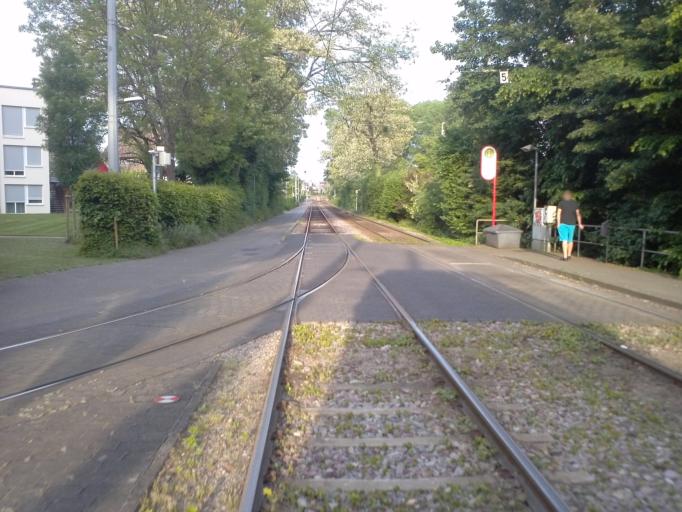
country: DE
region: Baden-Wuerttemberg
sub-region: Karlsruhe Region
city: Rheinstetten
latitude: 49.0044
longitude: 8.3227
